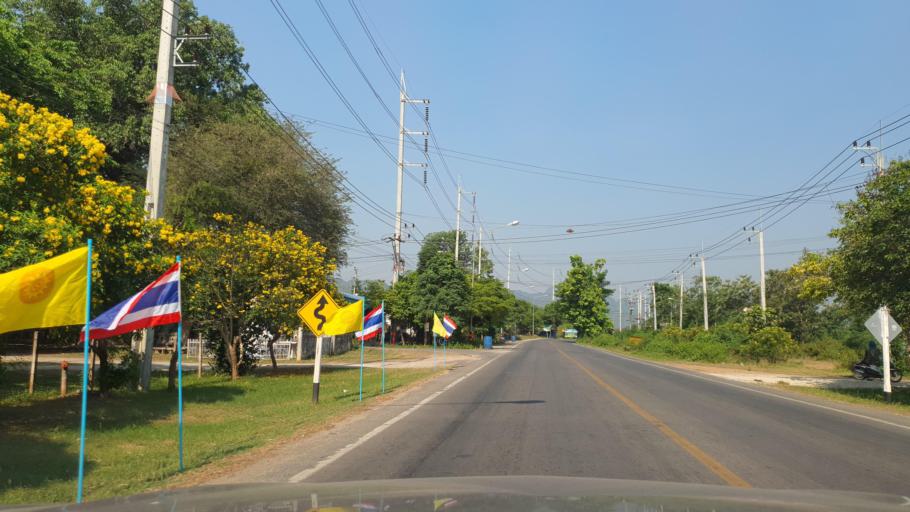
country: TH
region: Kanchanaburi
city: Kanchanaburi
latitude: 14.0371
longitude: 99.4816
